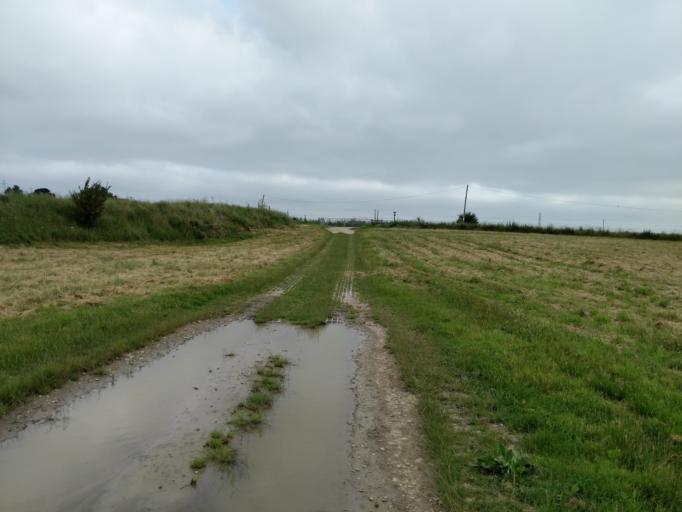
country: GB
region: England
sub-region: Kent
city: Faversham
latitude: 51.3294
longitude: 0.9170
